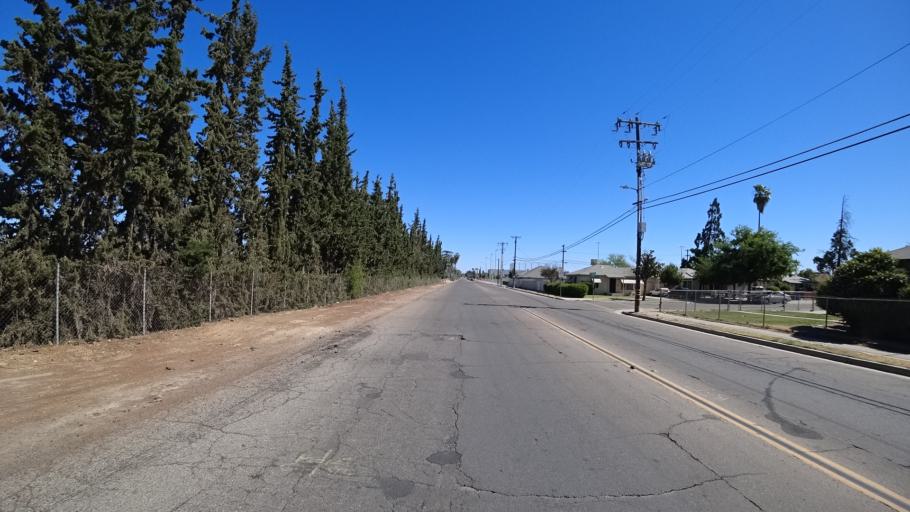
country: US
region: California
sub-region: Fresno County
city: Fresno
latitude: 36.7094
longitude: -119.7999
